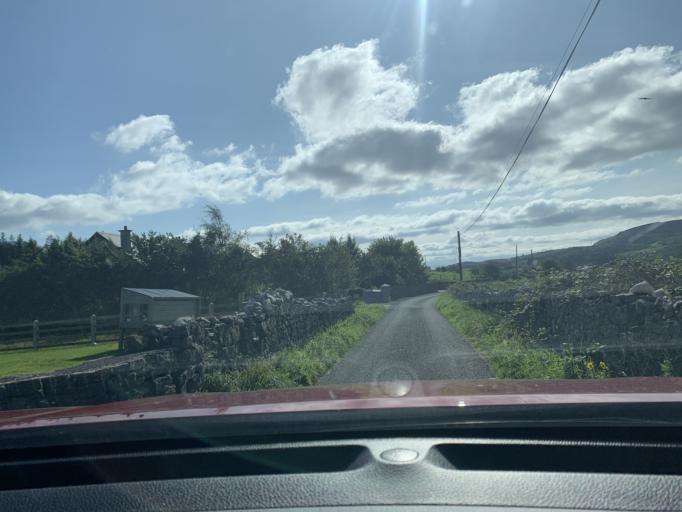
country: IE
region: Connaught
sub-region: Roscommon
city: Boyle
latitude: 54.0814
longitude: -8.3680
